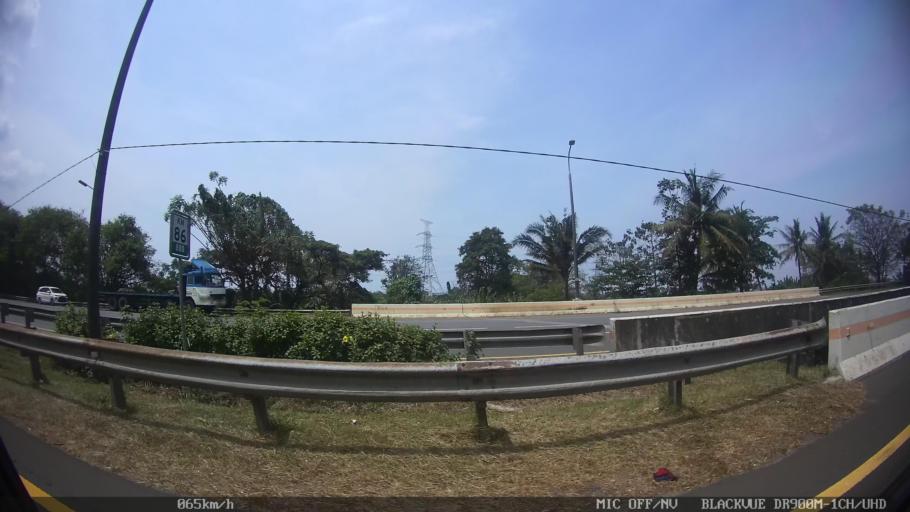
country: ID
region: Banten
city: Bojonegara
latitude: -6.0229
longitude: 106.0933
